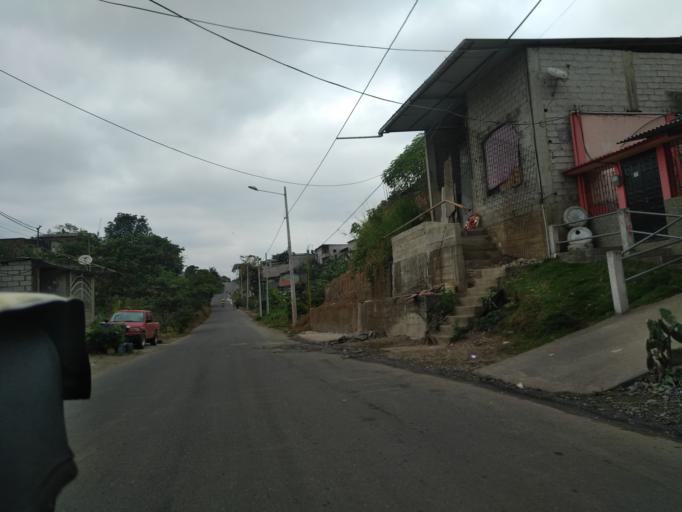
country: EC
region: Los Rios
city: Quevedo
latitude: -1.0233
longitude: -79.4386
